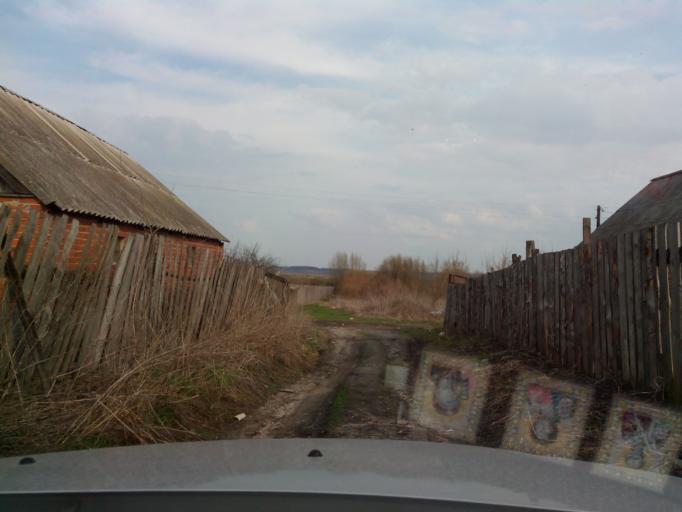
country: RU
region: Rjazan
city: Spassk-Ryazanskiy
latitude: 54.4403
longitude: 40.3862
